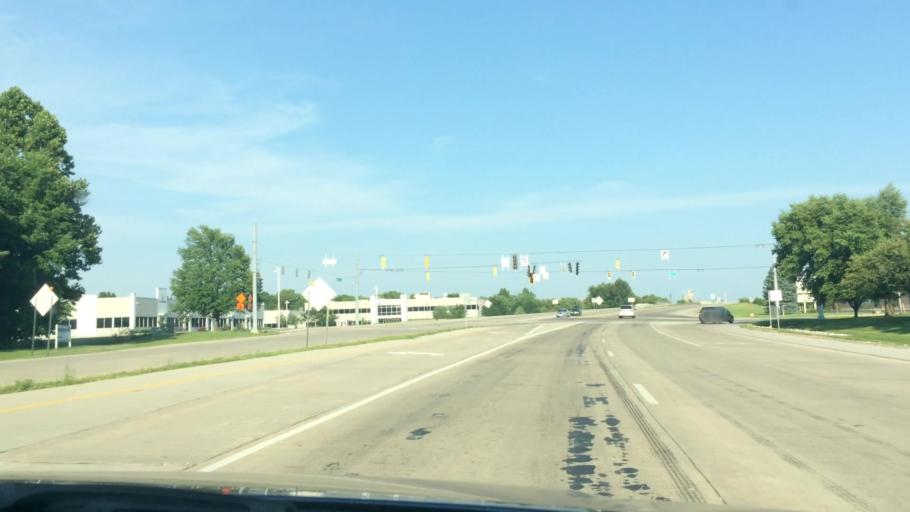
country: US
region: Indiana
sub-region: Tippecanoe County
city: Lafayette
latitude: 40.4500
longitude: -86.8816
